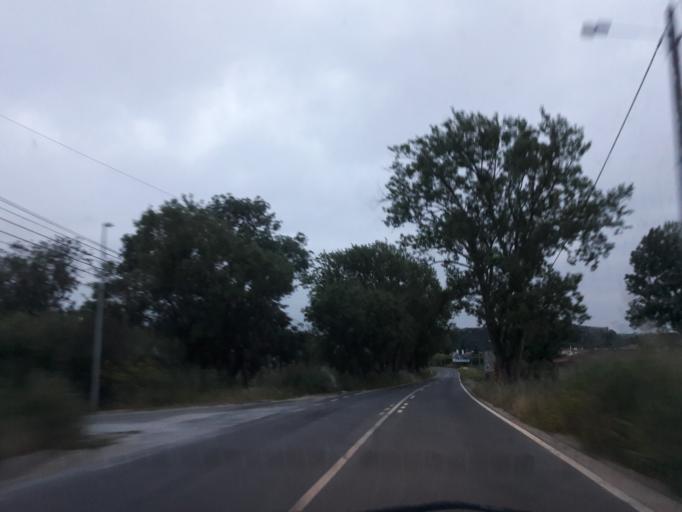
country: PT
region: Leiria
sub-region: Obidos
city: Obidos
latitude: 39.3677
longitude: -9.1458
